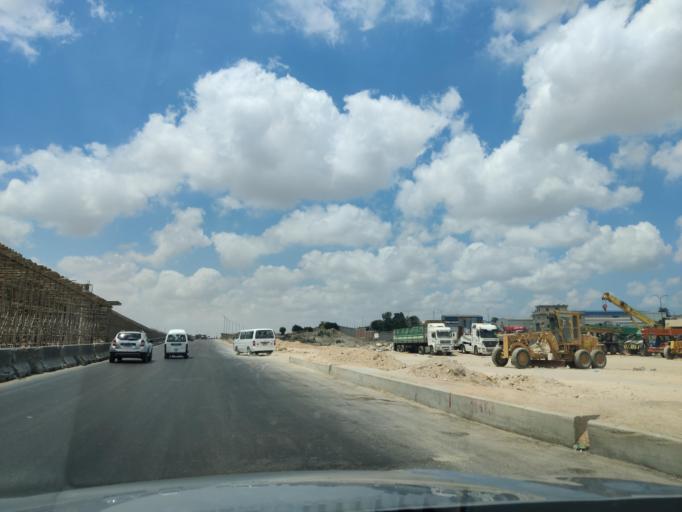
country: EG
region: Alexandria
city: Alexandria
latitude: 31.0318
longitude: 29.7839
